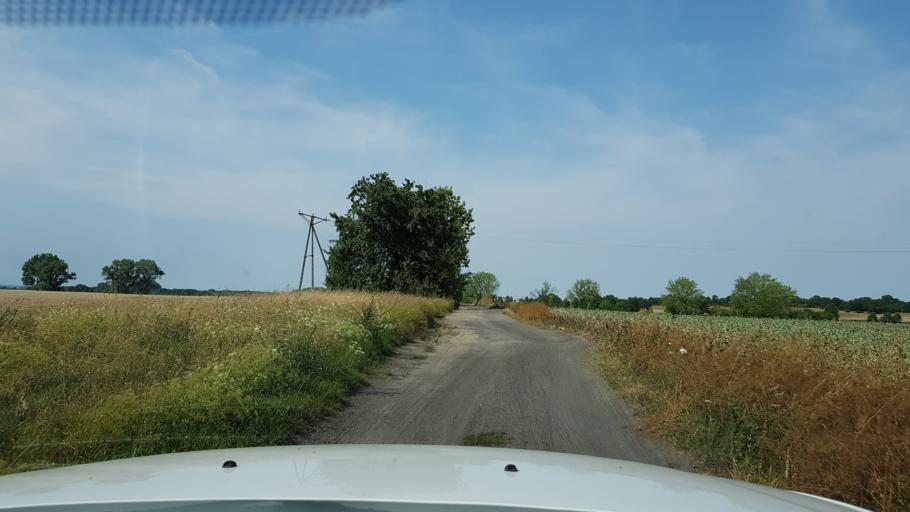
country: PL
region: West Pomeranian Voivodeship
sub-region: Powiat pyrzycki
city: Pyrzyce
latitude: 53.1136
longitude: 14.8846
